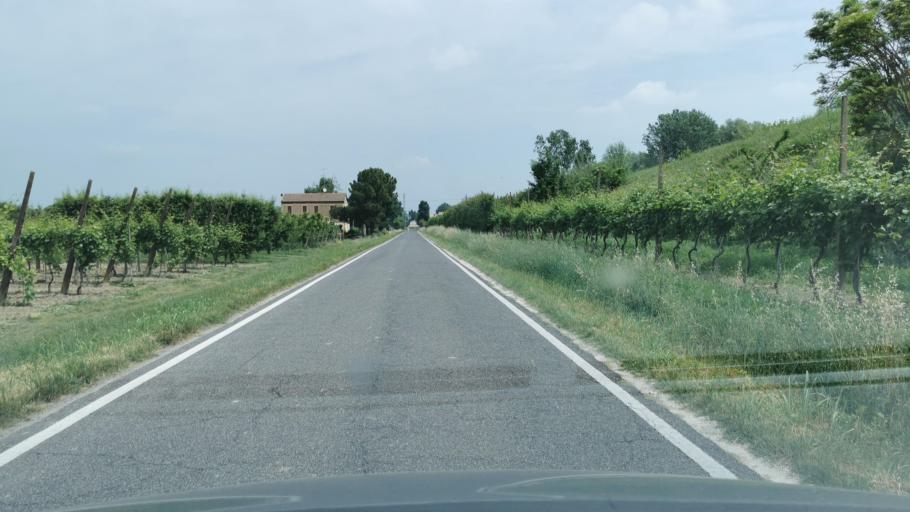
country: IT
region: Emilia-Romagna
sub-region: Provincia di Ravenna
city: Russi
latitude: 44.3943
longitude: 12.0152
